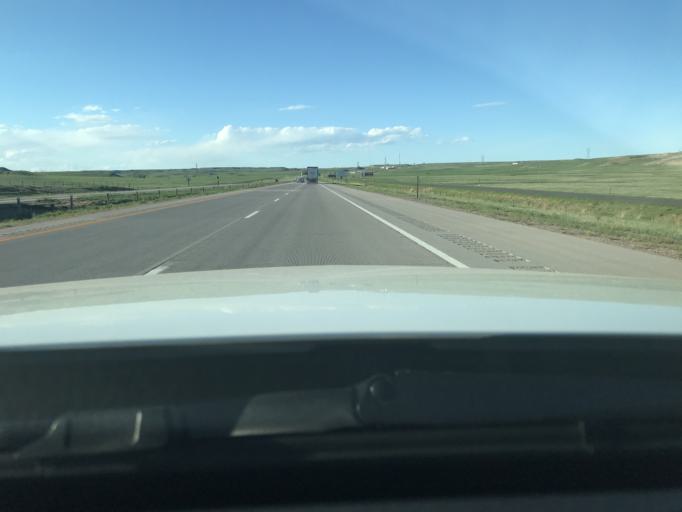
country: US
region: Wyoming
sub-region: Laramie County
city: South Greeley
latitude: 41.0096
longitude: -104.9049
